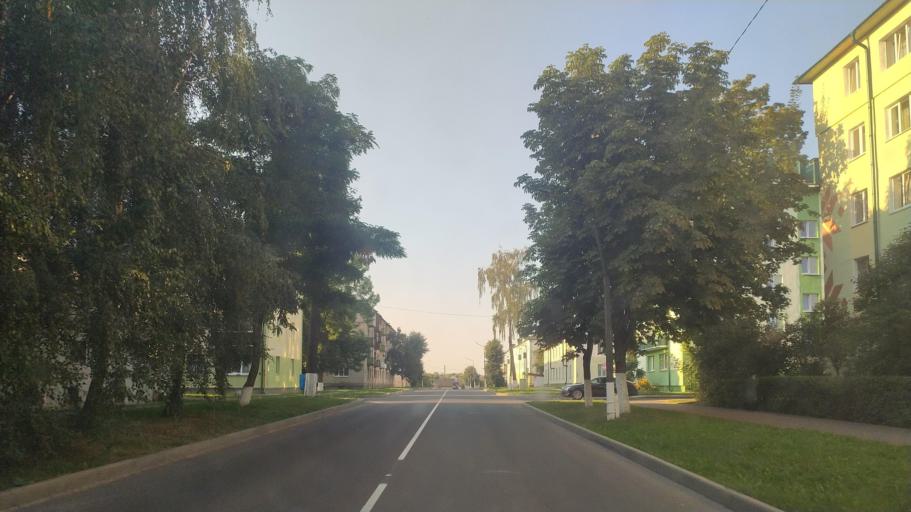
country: BY
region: Brest
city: Byaroza
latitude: 52.5418
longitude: 24.9843
